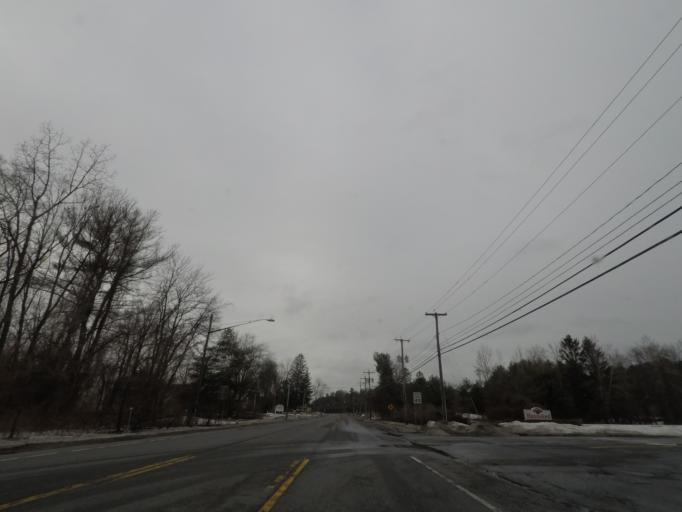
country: US
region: New York
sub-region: Albany County
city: Voorheesville
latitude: 42.7157
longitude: -73.9345
